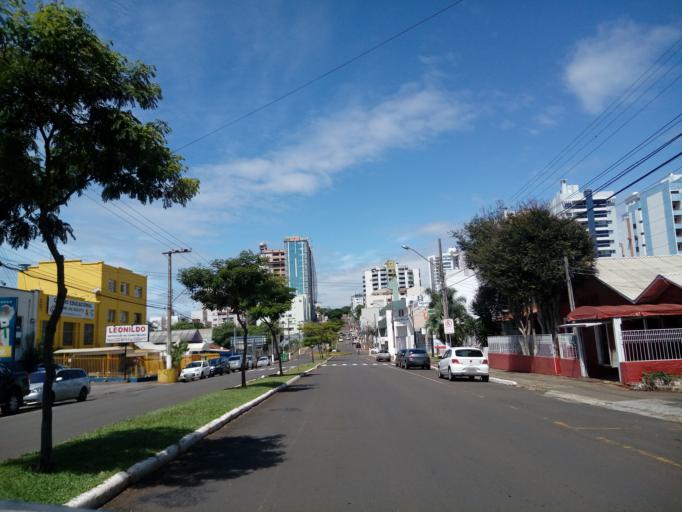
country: BR
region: Santa Catarina
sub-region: Chapeco
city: Chapeco
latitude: -27.1044
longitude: -52.6108
